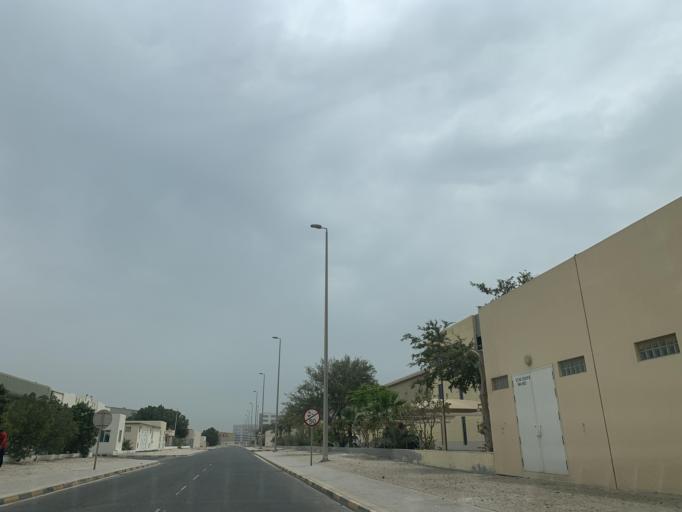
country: BH
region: Muharraq
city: Al Hadd
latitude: 26.2145
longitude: 50.6627
